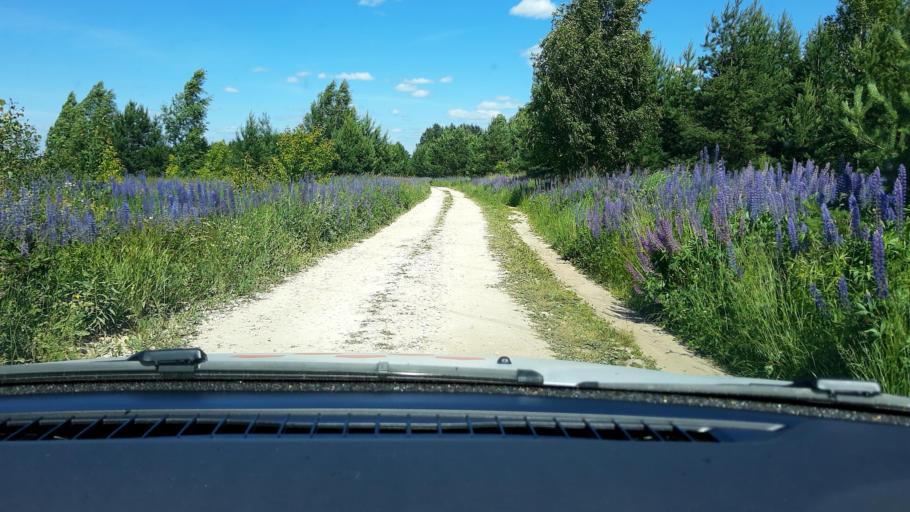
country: RU
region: Nizjnij Novgorod
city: Surovatikha
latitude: 55.8728
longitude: 43.9758
